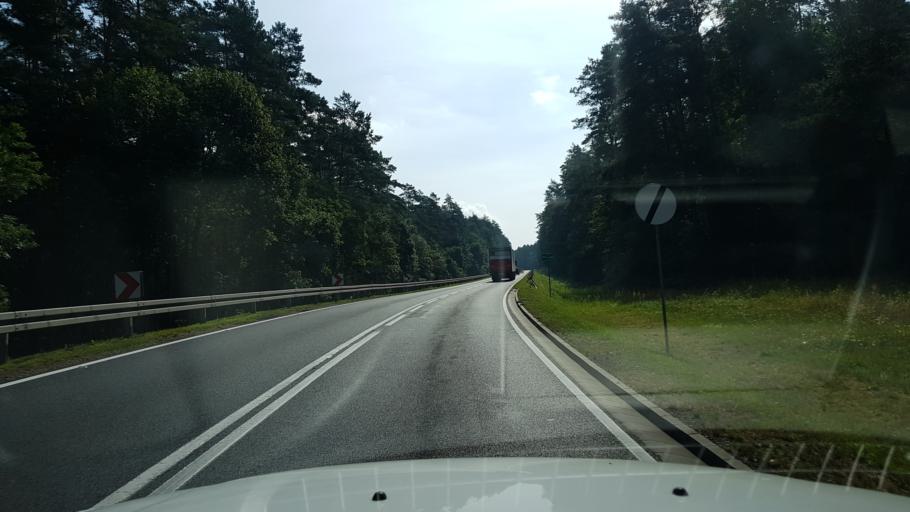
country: PL
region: West Pomeranian Voivodeship
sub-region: Powiat walecki
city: Miroslawiec
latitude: 53.3498
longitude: 16.1653
